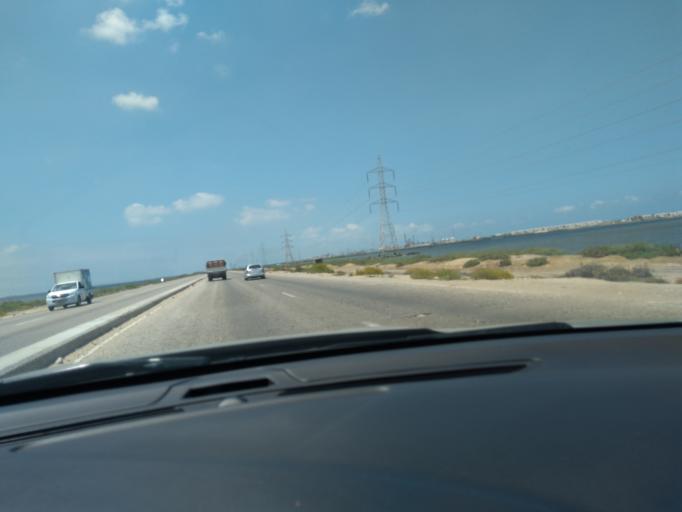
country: EG
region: Muhafazat Bur Sa`id
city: Port Said
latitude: 31.2825
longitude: 32.1865
